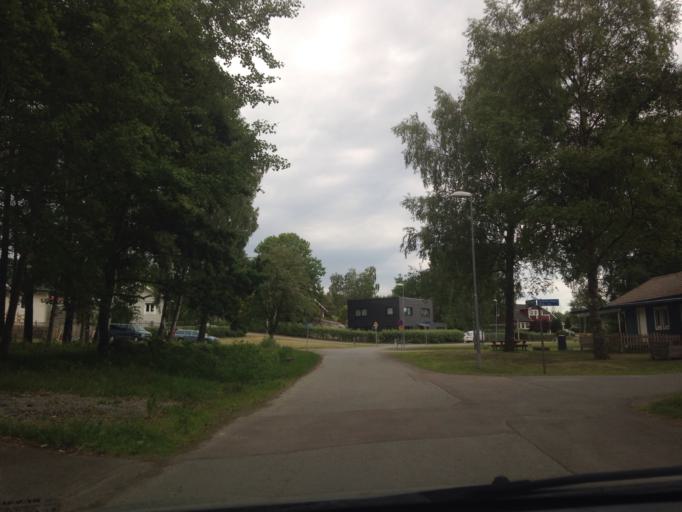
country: SE
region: Vaestra Goetaland
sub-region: Goteborg
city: Torslanda
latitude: 57.7701
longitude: 11.8419
